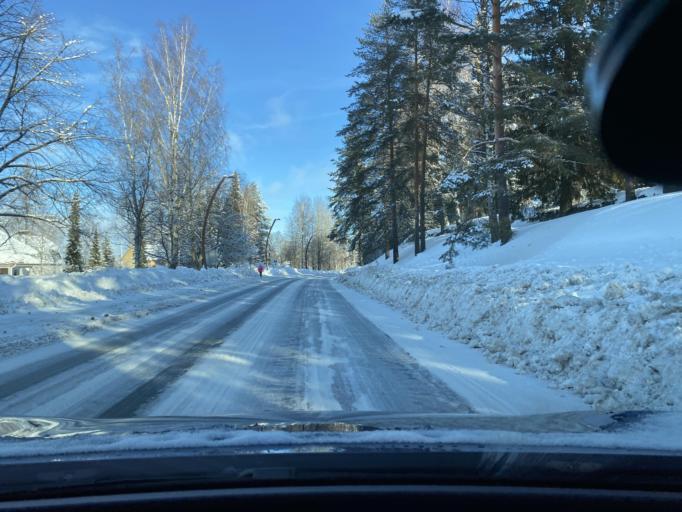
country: FI
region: Southern Savonia
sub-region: Mikkeli
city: Kangasniemi
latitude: 61.9921
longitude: 26.6445
